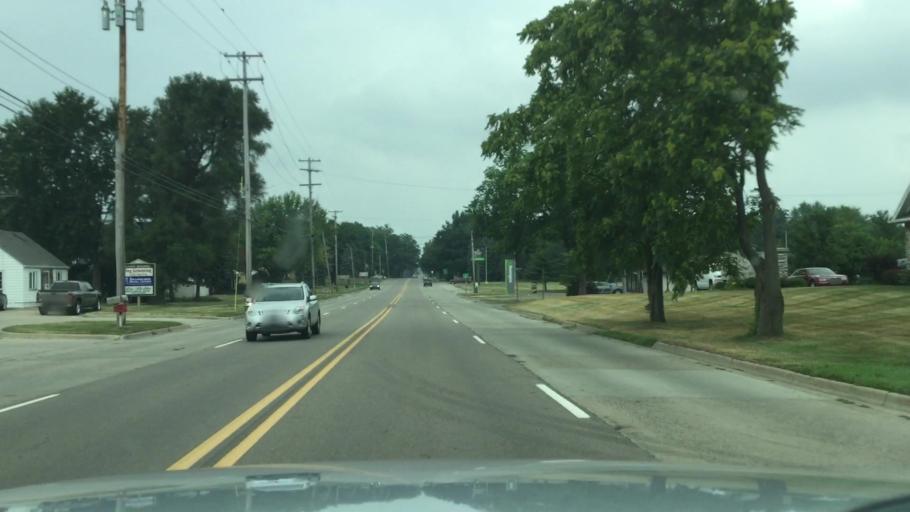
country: US
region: Michigan
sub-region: Shiawassee County
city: Owosso
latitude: 43.0155
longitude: -84.1768
